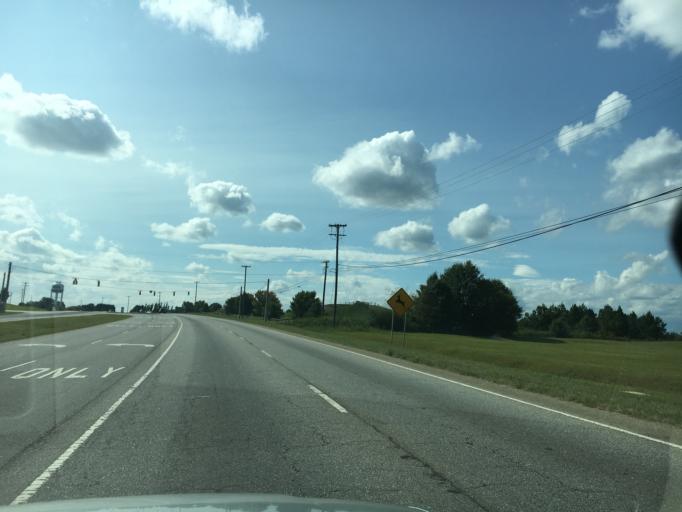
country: US
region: South Carolina
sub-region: Spartanburg County
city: Duncan
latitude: 34.9028
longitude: -82.1728
